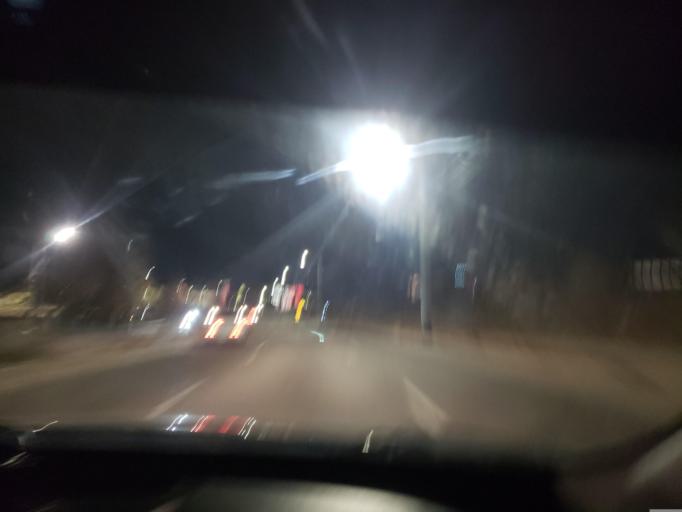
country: US
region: New Mexico
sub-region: Bernalillo County
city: Albuquerque
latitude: 35.0695
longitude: -106.6261
